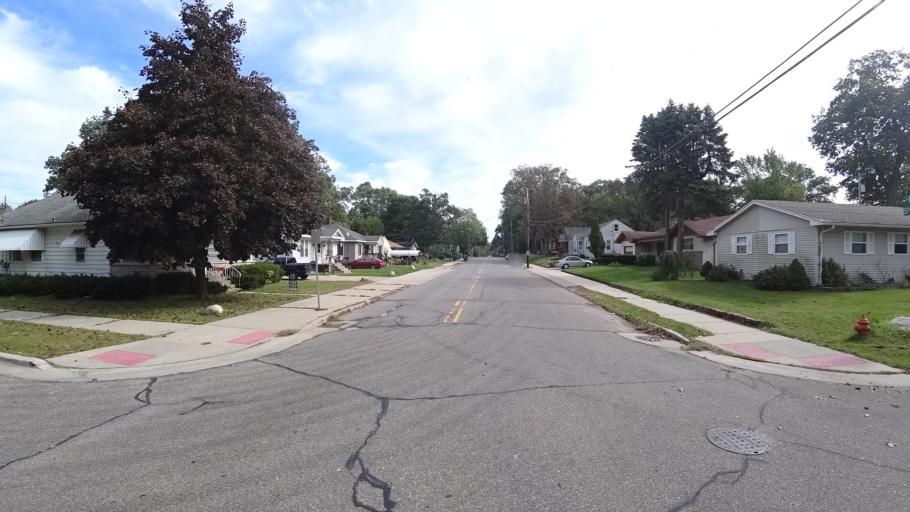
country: US
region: Indiana
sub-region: LaPorte County
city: Michigan City
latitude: 41.7169
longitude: -86.8788
